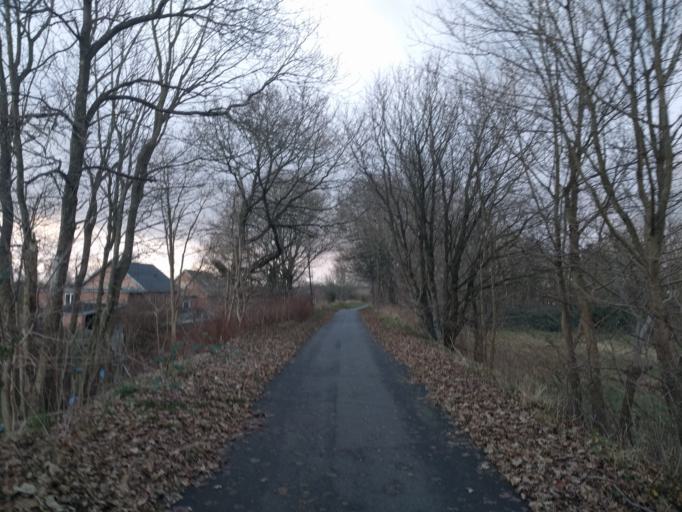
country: DK
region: Central Jutland
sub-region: Viborg Kommune
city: Viborg
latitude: 56.4339
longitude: 9.3971
